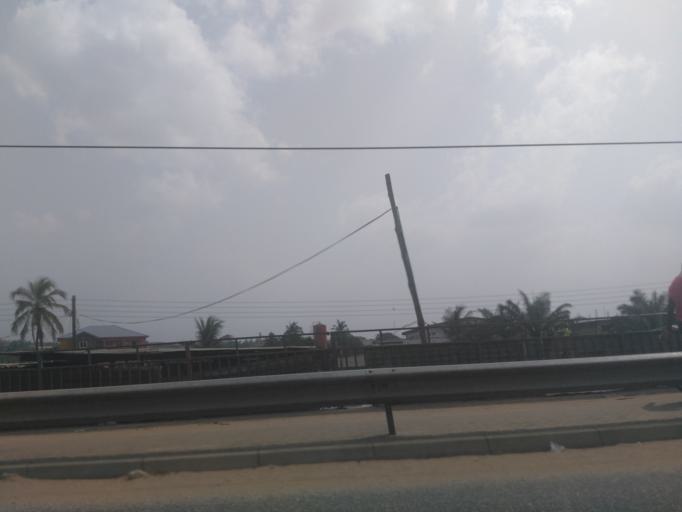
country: GH
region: Greater Accra
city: Dome
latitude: 5.6071
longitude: -0.2260
